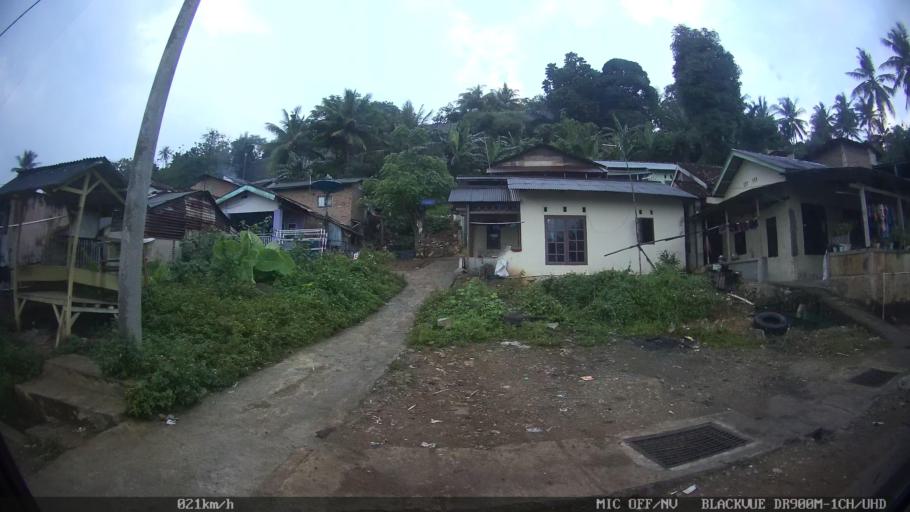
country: ID
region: Lampung
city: Bandarlampung
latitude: -5.4367
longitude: 105.2794
